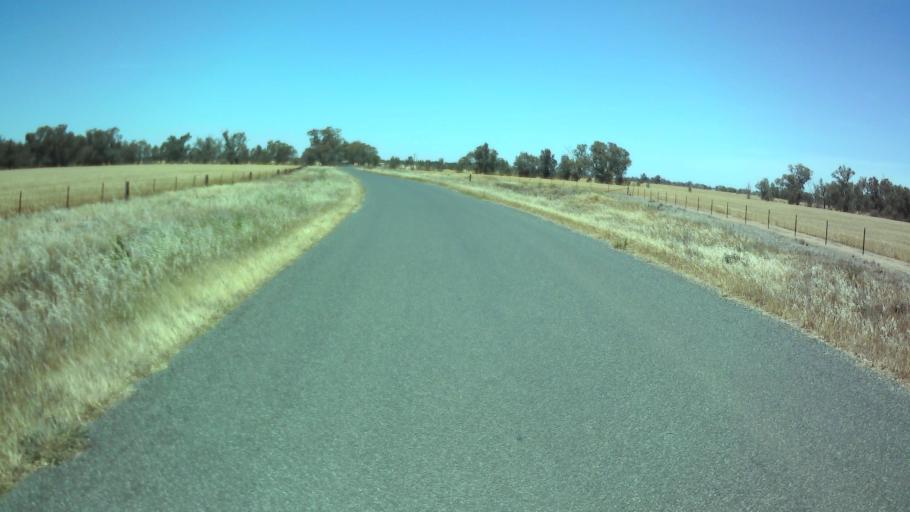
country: AU
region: New South Wales
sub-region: Weddin
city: Grenfell
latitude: -34.0359
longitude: 147.7897
